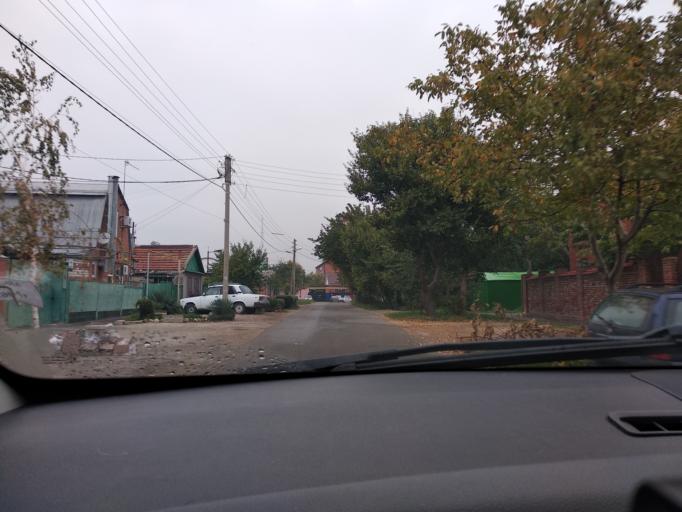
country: RU
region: Krasnodarskiy
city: Krasnodar
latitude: 45.0163
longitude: 39.0002
